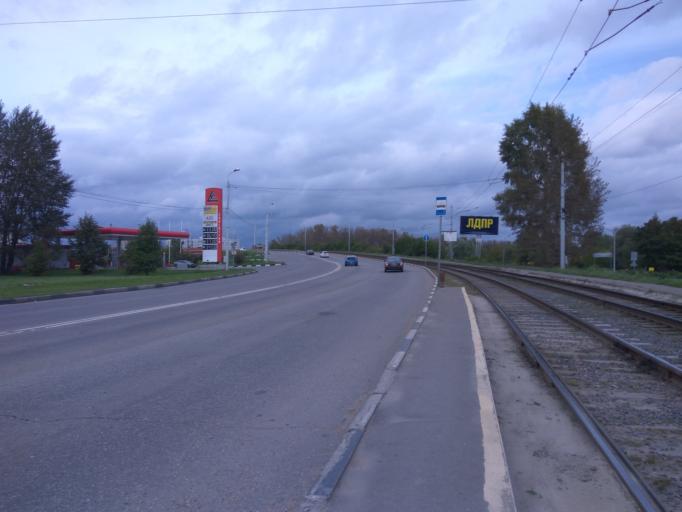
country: RU
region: Moskovskaya
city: Kolomna
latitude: 55.0693
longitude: 38.7584
